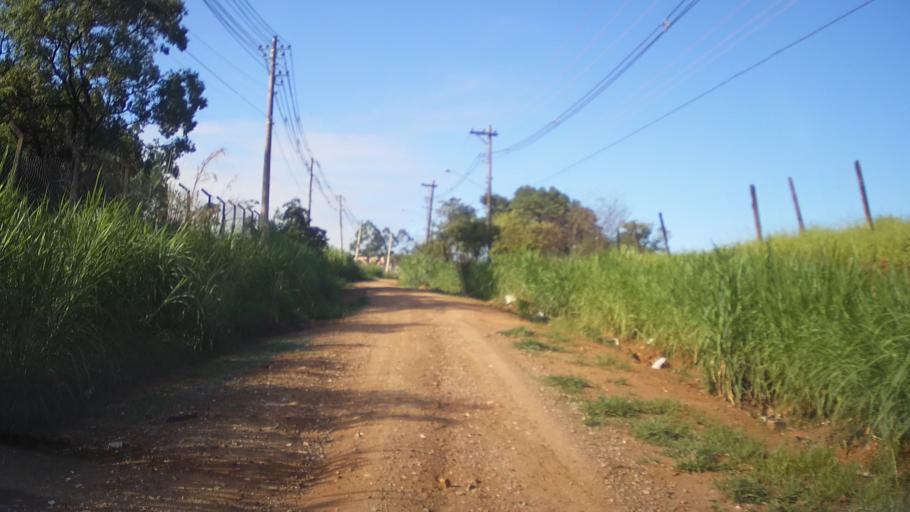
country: BR
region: Sao Paulo
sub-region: Itupeva
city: Itupeva
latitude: -23.1831
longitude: -46.9787
